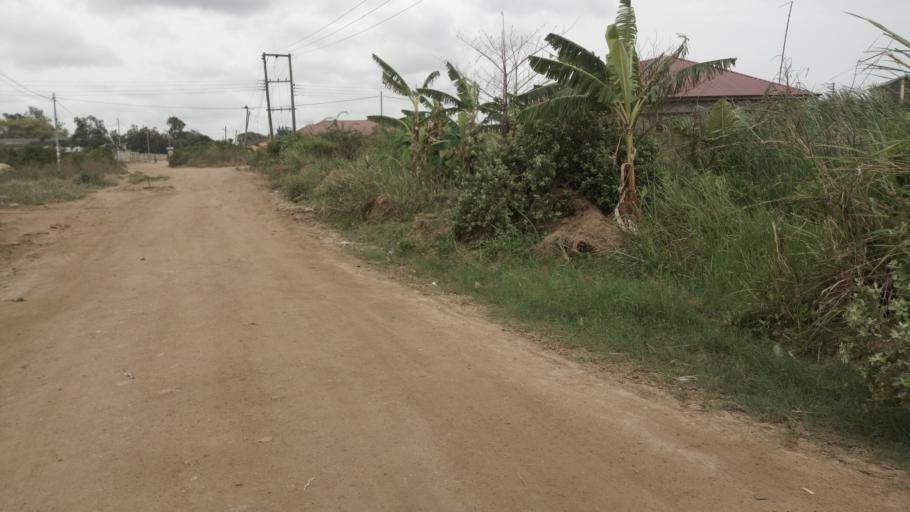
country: GH
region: Central
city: Winneba
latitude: 5.3652
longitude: -0.6402
